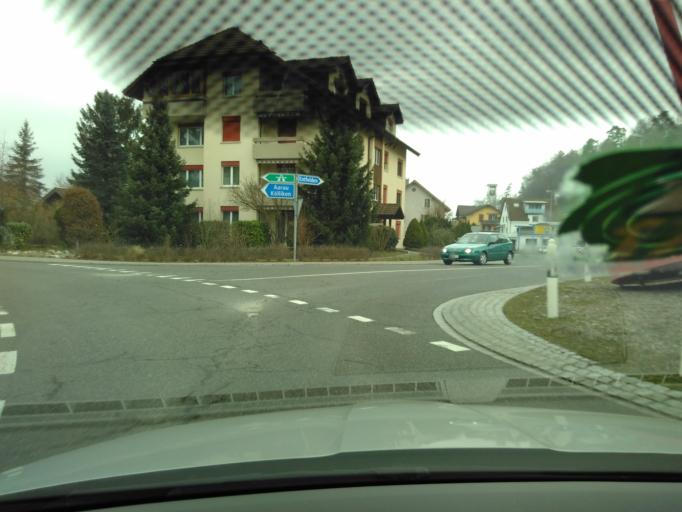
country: CH
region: Aargau
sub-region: Bezirk Aarau
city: Muhen
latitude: 47.3324
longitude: 8.0557
